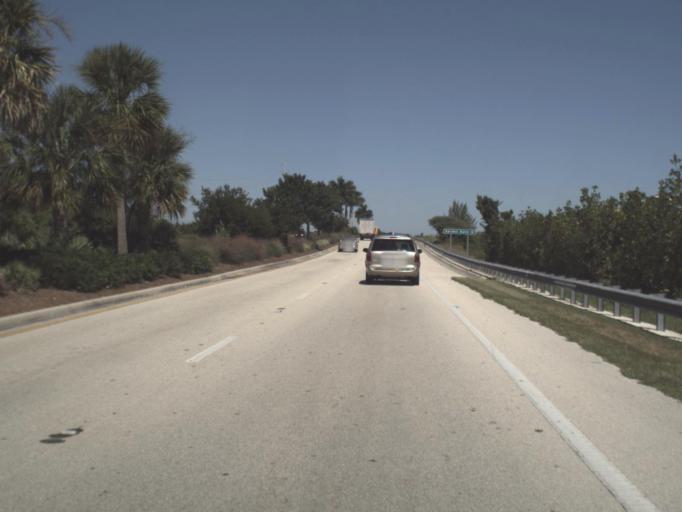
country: US
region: Florida
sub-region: Collier County
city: Marco
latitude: 25.9851
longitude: -81.7023
